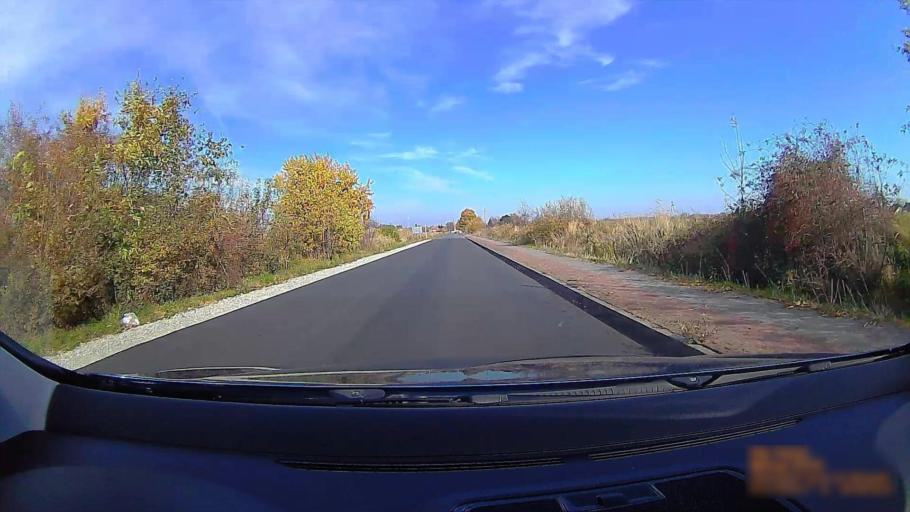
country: PL
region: Greater Poland Voivodeship
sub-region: Powiat ostrzeszowski
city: Doruchow
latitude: 51.4066
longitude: 18.0707
